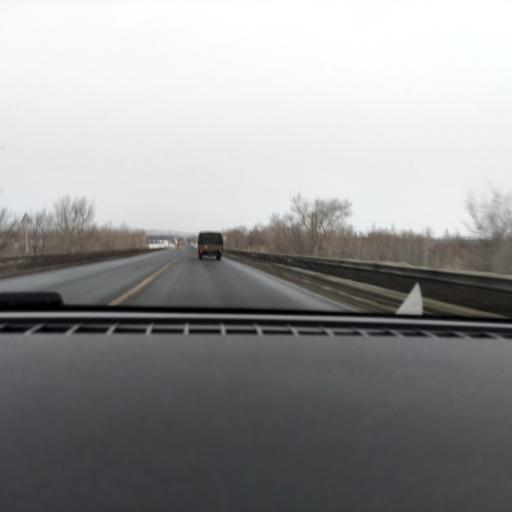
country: RU
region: Samara
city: Kinel'
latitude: 53.1882
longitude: 50.5158
